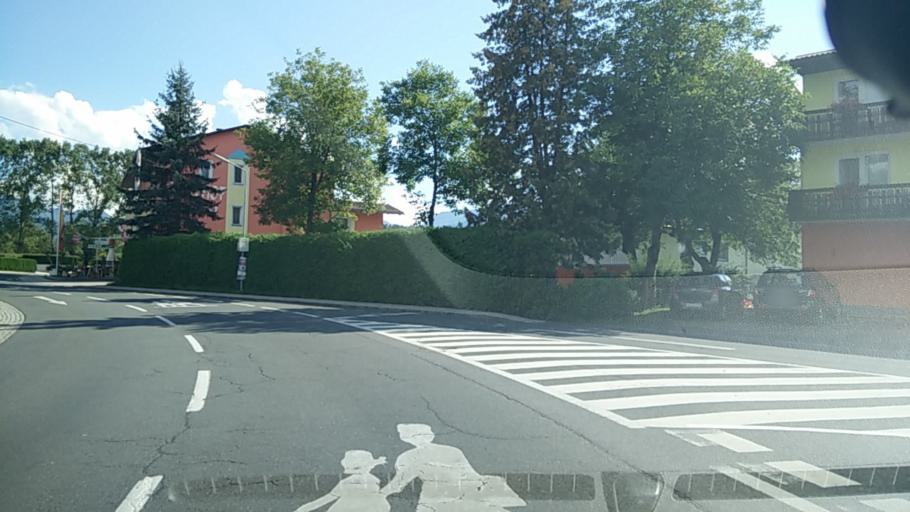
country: AT
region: Carinthia
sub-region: Politischer Bezirk Volkermarkt
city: Sittersdorf
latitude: 46.5795
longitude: 14.5637
